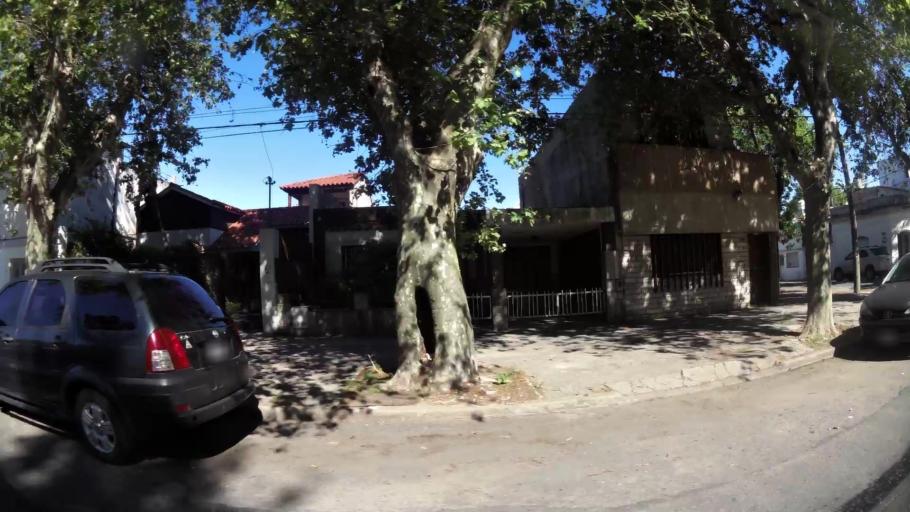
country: AR
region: Santa Fe
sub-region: Departamento de Rosario
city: Rosario
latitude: -32.9508
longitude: -60.6822
